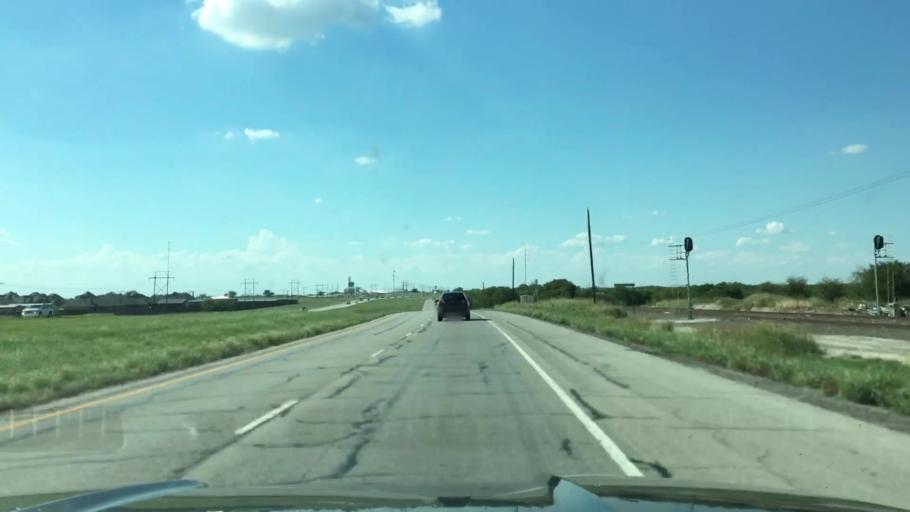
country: US
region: Texas
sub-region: Wise County
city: Decatur
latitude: 33.1702
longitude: -97.5365
